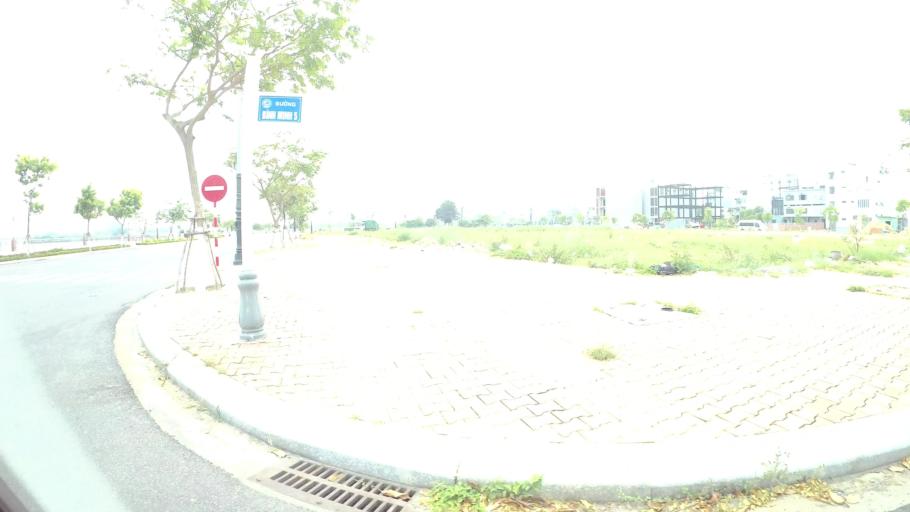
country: VN
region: Da Nang
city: Son Tra
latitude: 16.0553
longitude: 108.2235
